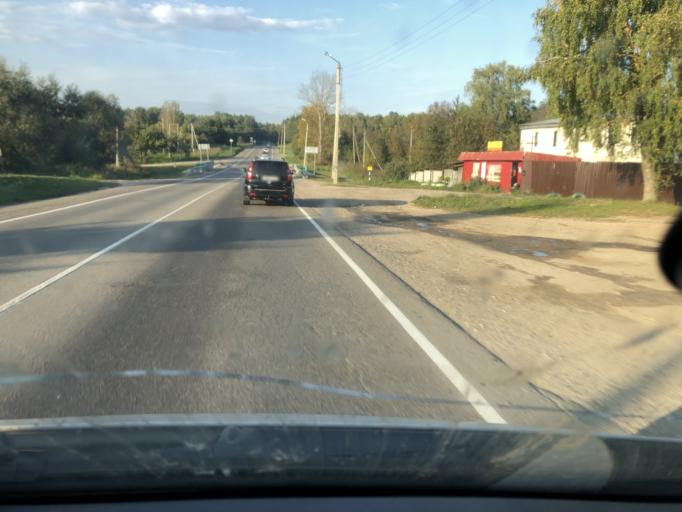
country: RU
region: Kaluga
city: Peremyshl'
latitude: 54.3827
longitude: 36.2010
